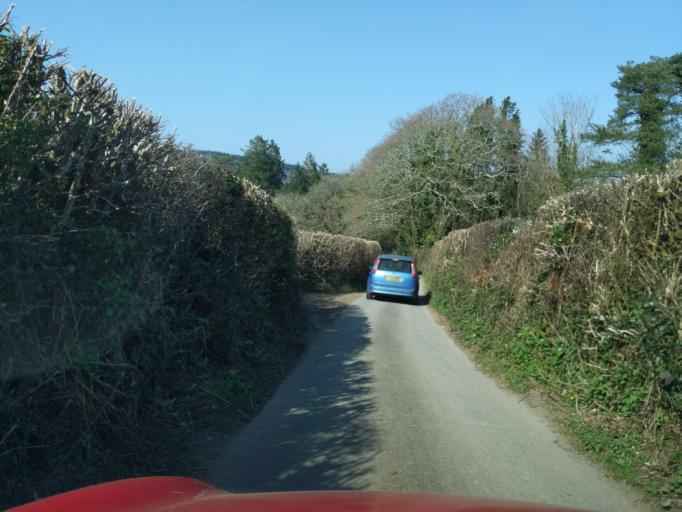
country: GB
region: England
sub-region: Devon
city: Bere Alston
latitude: 50.4534
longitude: -4.1512
